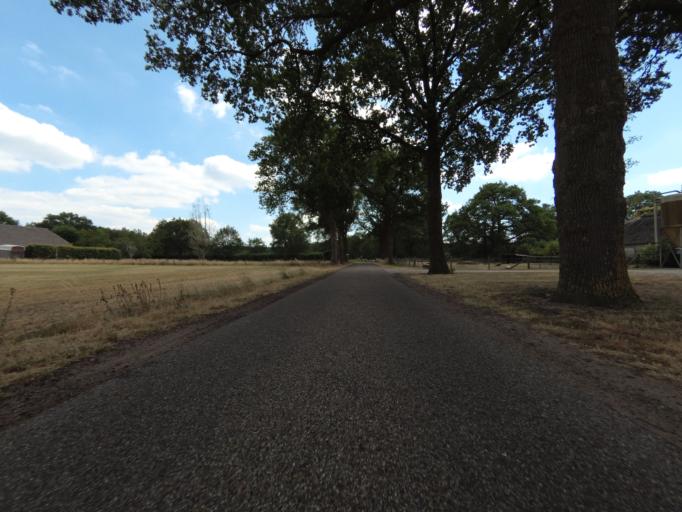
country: NL
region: Overijssel
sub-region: Gemeente Raalte
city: Raalte
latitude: 52.3202
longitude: 6.3663
